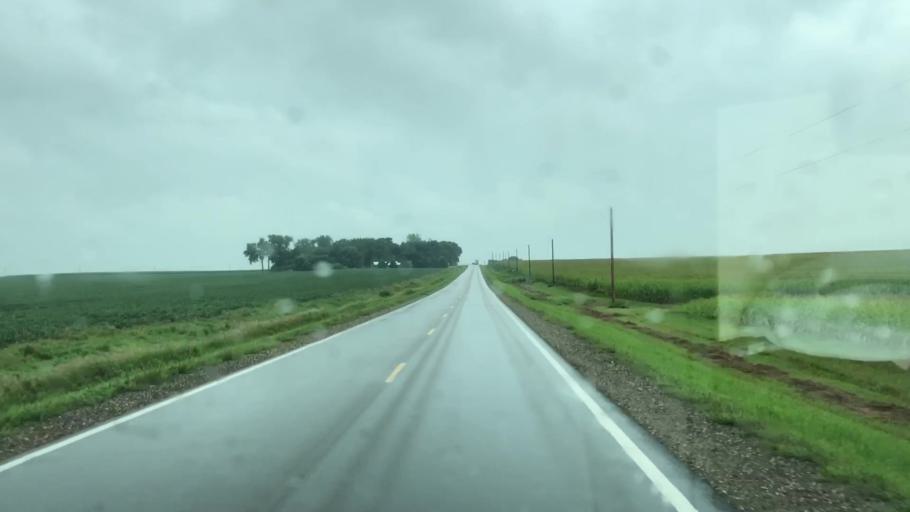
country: US
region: Iowa
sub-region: O'Brien County
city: Sanborn
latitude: 43.2651
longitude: -95.7237
